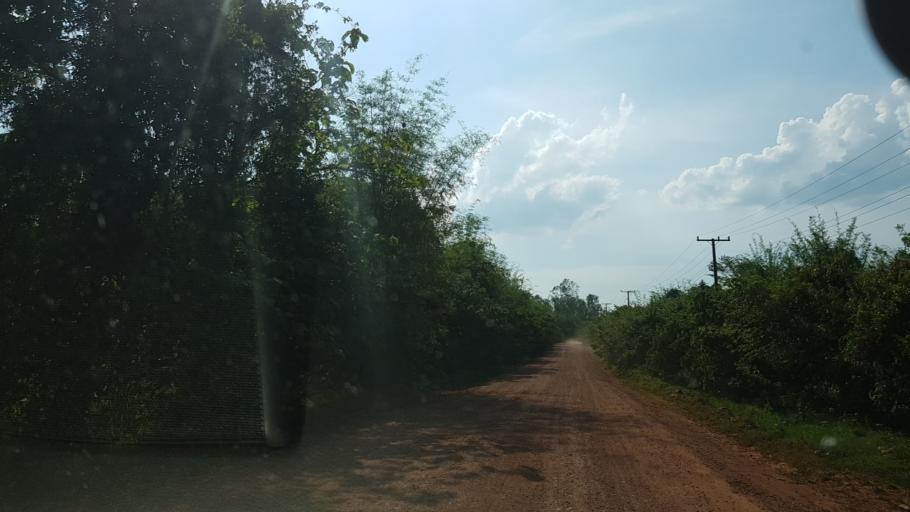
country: LA
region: Vientiane
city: Muang Phon-Hong
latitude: 18.3445
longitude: 102.2910
